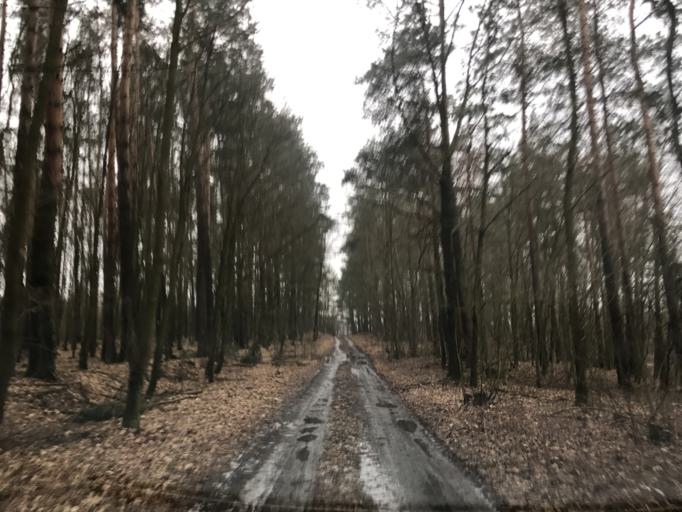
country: PL
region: Kujawsko-Pomorskie
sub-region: Powiat brodnicki
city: Brzozie
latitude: 53.2906
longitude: 19.5642
